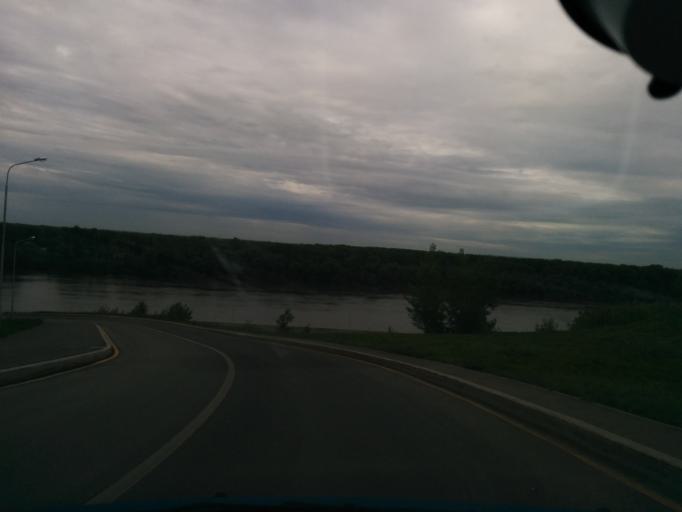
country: RU
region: Bashkortostan
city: Ufa
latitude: 54.7172
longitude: 55.9287
